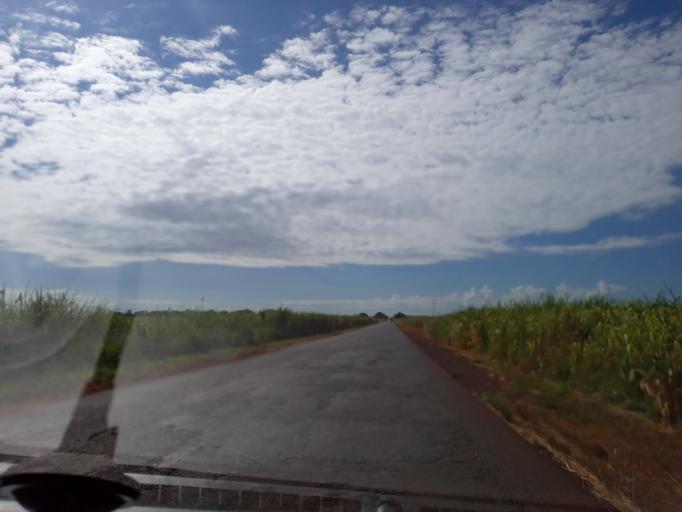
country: BR
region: Goias
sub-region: Itumbiara
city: Itumbiara
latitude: -18.4594
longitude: -49.1411
